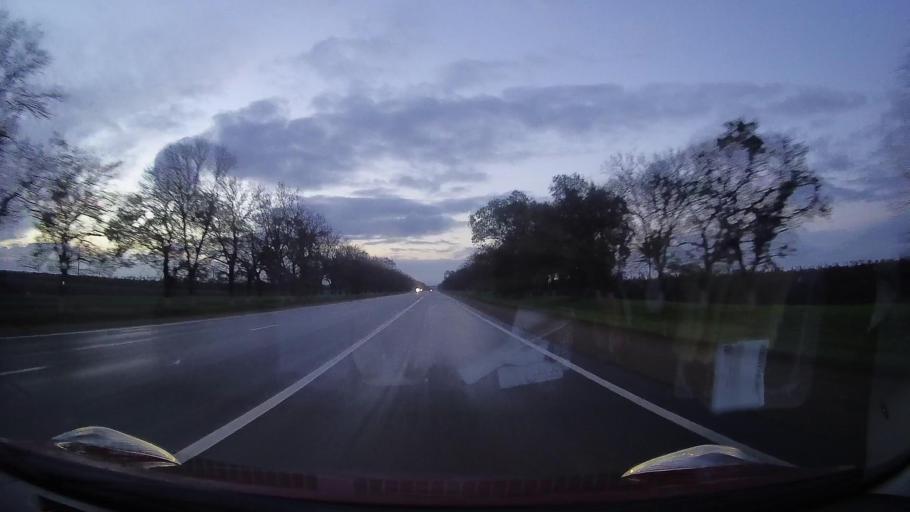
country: RU
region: Krasnodarskiy
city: Zavetnyy
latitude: 44.8995
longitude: 41.1875
